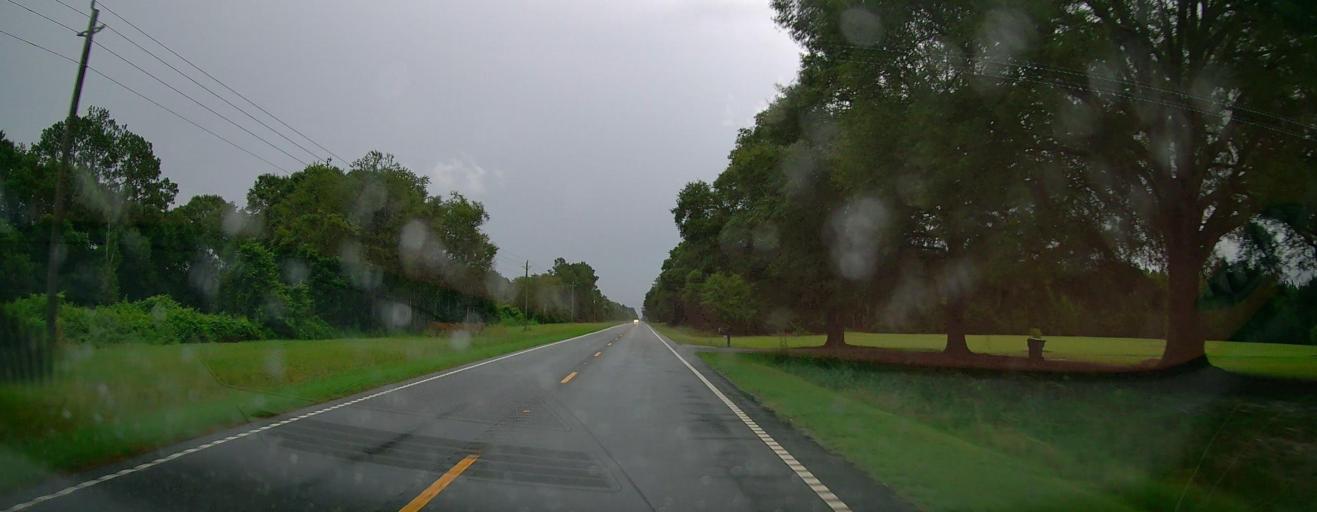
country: US
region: Georgia
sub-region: Brantley County
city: Nahunta
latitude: 31.3429
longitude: -81.9913
